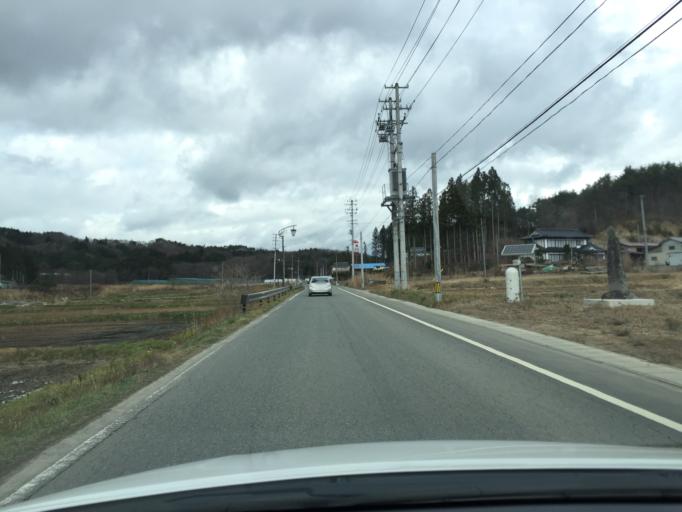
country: JP
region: Fukushima
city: Yanagawamachi-saiwaicho
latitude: 37.7039
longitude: 140.6963
